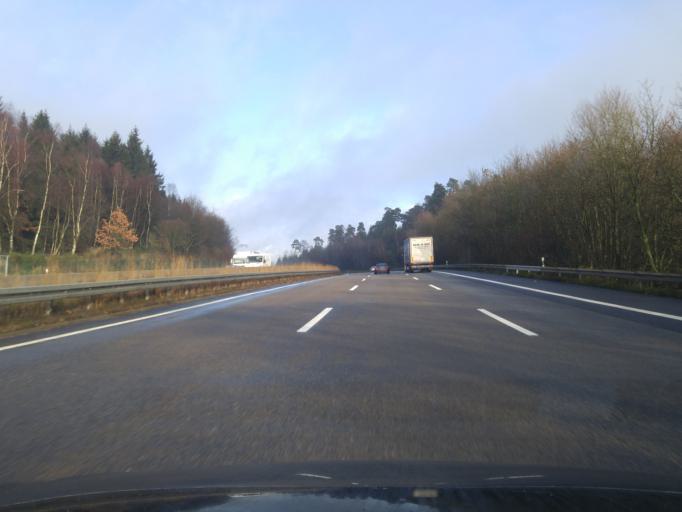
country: DE
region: Hesse
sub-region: Regierungsbezirk Kassel
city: Kirchheim
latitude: 50.8730
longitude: 9.5980
